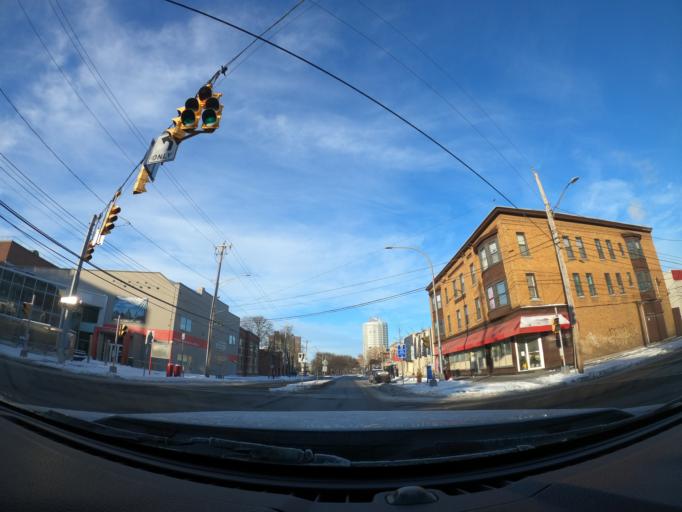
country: US
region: New York
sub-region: Onondaga County
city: Syracuse
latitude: 43.0470
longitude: -76.1378
